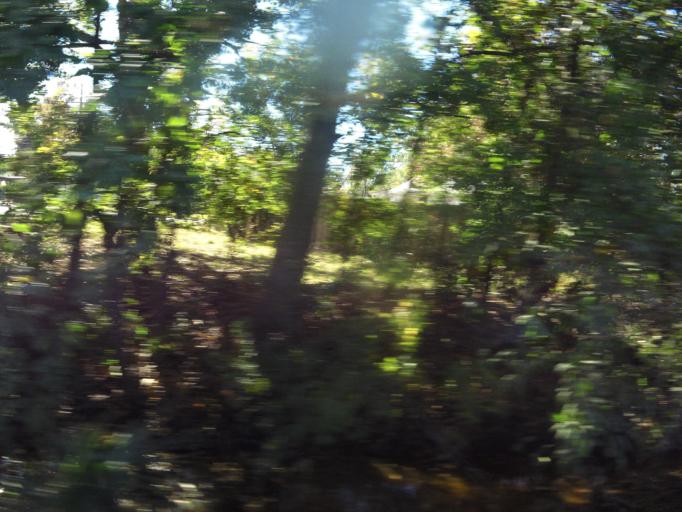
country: US
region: Georgia
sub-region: Chatham County
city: Savannah
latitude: 32.0613
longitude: -81.1359
